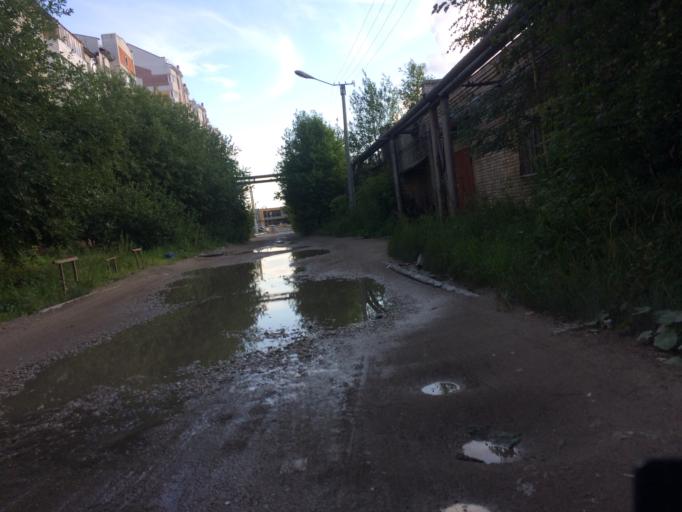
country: RU
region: Mariy-El
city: Yoshkar-Ola
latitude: 56.6350
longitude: 47.9374
